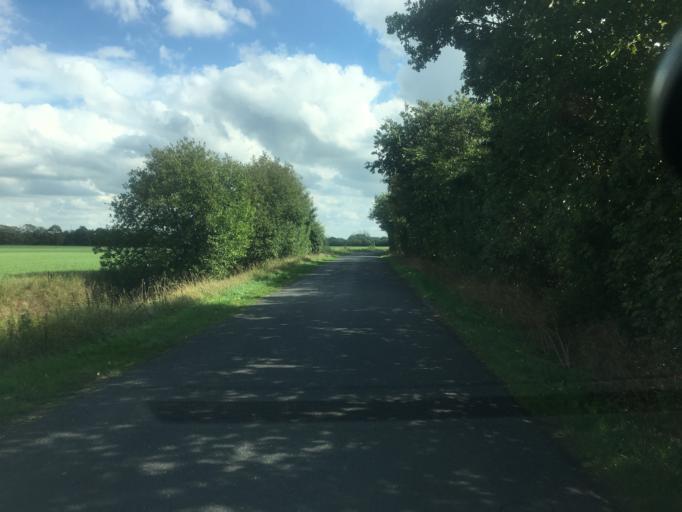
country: DK
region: South Denmark
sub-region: Tonder Kommune
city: Logumkloster
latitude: 55.0056
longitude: 9.0109
